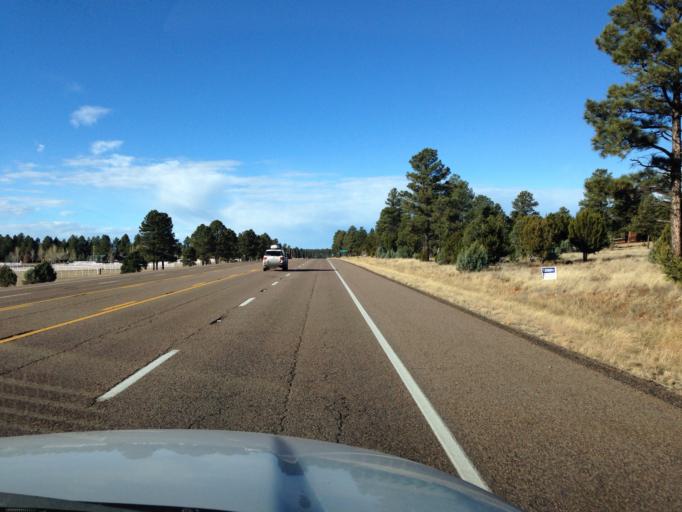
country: US
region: Arizona
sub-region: Navajo County
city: Heber-Overgaard
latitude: 34.3921
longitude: -110.5303
